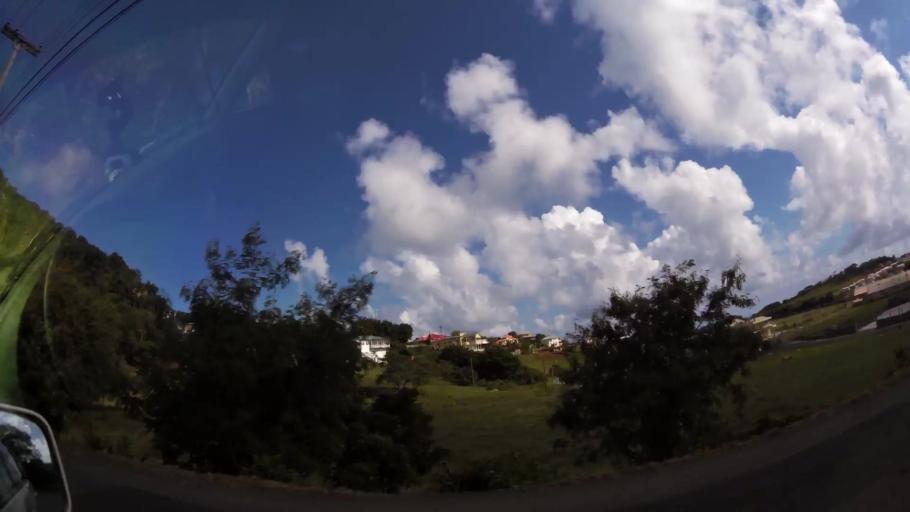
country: VC
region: Saint George
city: Kingstown
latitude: 13.1439
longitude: -61.1702
